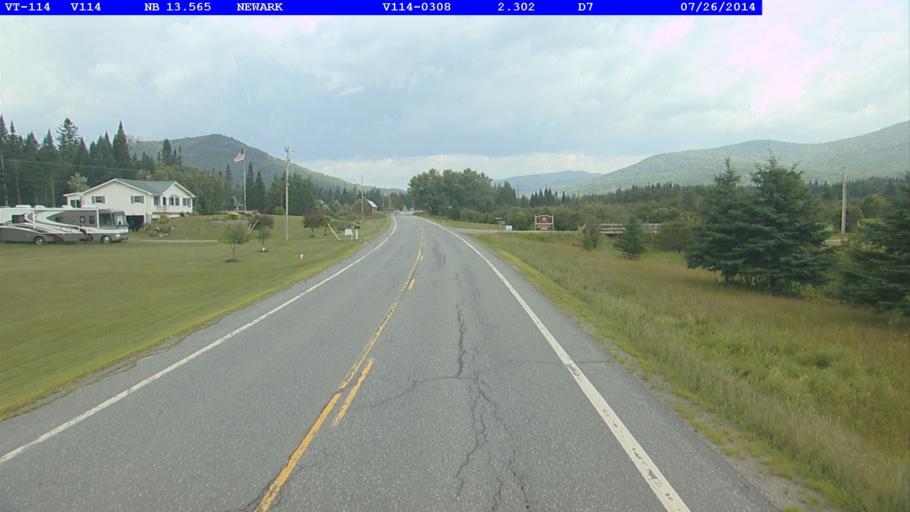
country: US
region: Vermont
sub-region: Caledonia County
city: Lyndonville
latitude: 44.7008
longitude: -71.8709
